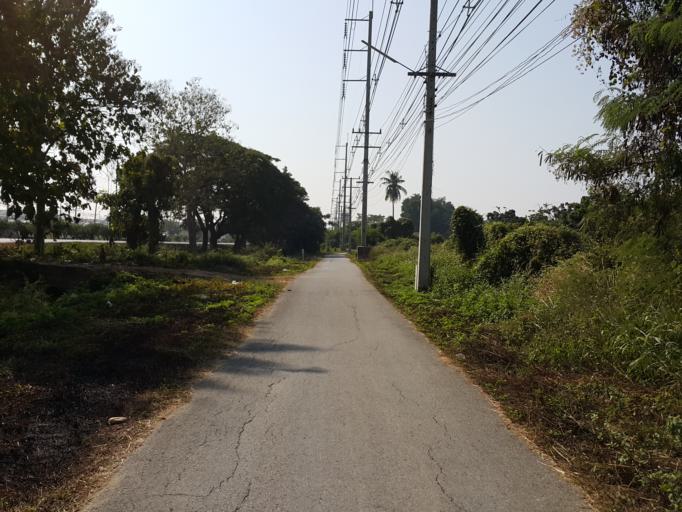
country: TH
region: Lamphun
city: Lamphun
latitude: 18.6224
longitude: 99.0472
